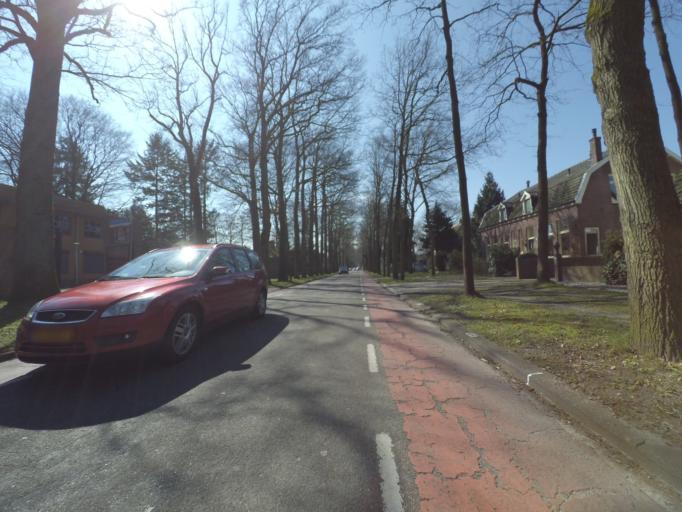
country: NL
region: Utrecht
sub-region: Gemeente Utrechtse Heuvelrug
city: Driebergen-Rijsenburg
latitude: 52.0542
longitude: 5.2736
